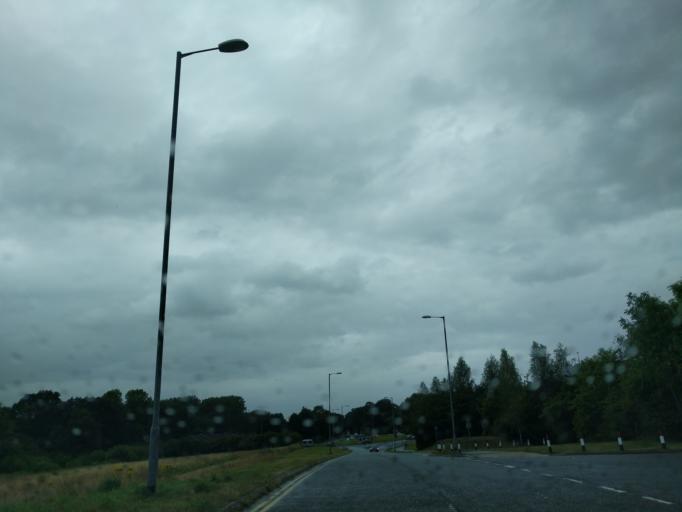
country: GB
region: England
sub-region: Staffordshire
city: Stafford
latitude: 52.8098
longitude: -2.0829
